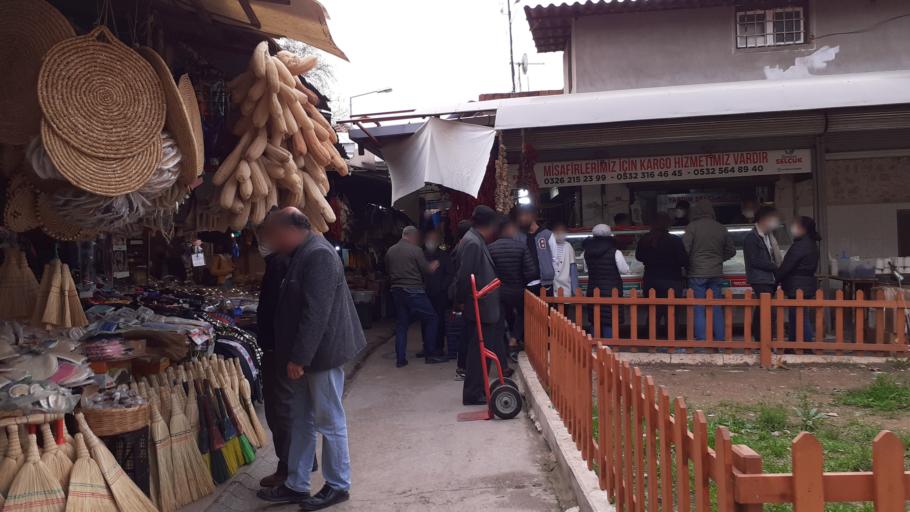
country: TR
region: Hatay
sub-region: Antakya Ilcesi
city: Antakya
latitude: 36.2038
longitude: 36.1642
